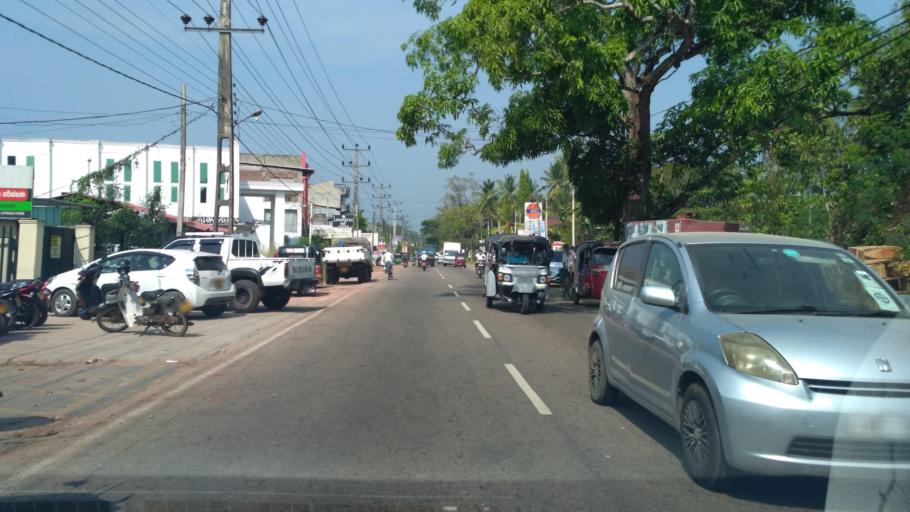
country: LK
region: North Western
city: Kuliyapitiya
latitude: 7.3301
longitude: 80.0191
